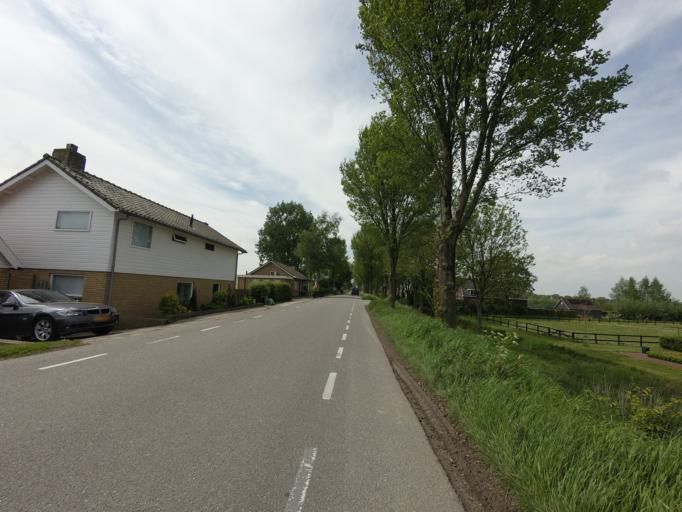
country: NL
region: South Holland
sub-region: Gemeente Binnenmaas
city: Mijnsheerenland
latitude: 51.7678
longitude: 4.4601
